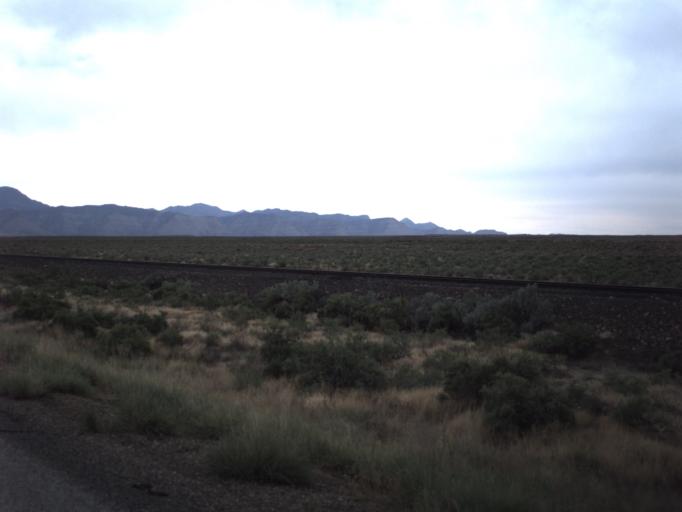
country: US
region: Utah
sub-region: Carbon County
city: East Carbon City
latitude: 39.5328
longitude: -110.5368
